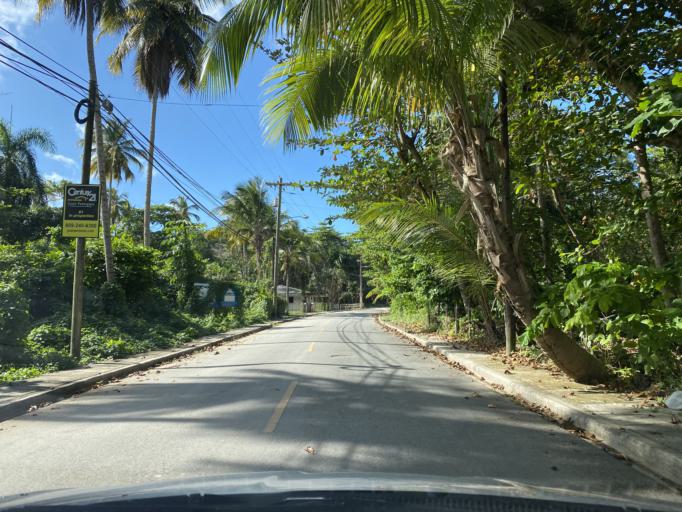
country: DO
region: Samana
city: Las Terrenas
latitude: 19.3115
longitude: -69.5704
